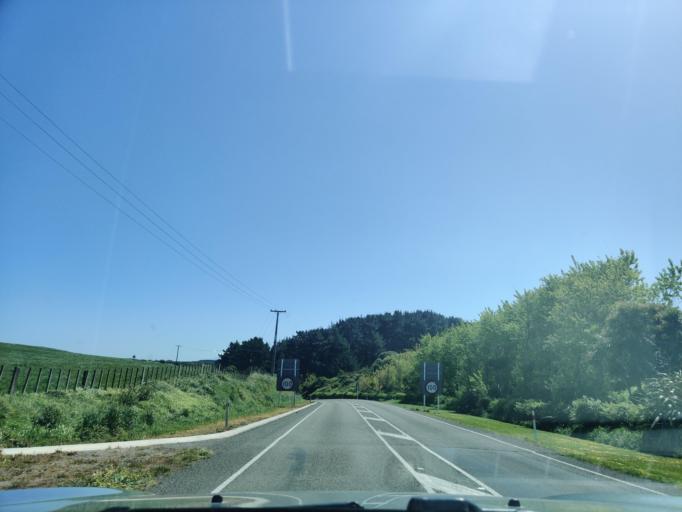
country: NZ
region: Taranaki
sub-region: South Taranaki District
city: Patea
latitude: -39.7078
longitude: 174.4470
